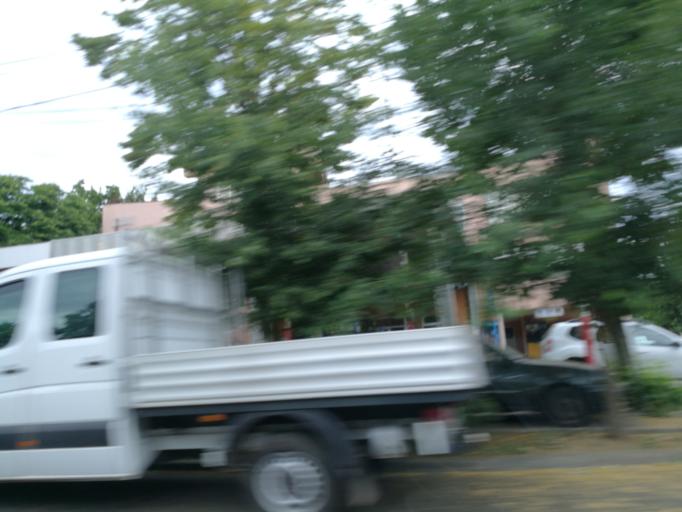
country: RO
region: Constanta
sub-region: Municipiul Constanta
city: Constanta
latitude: 44.1993
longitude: 28.6313
